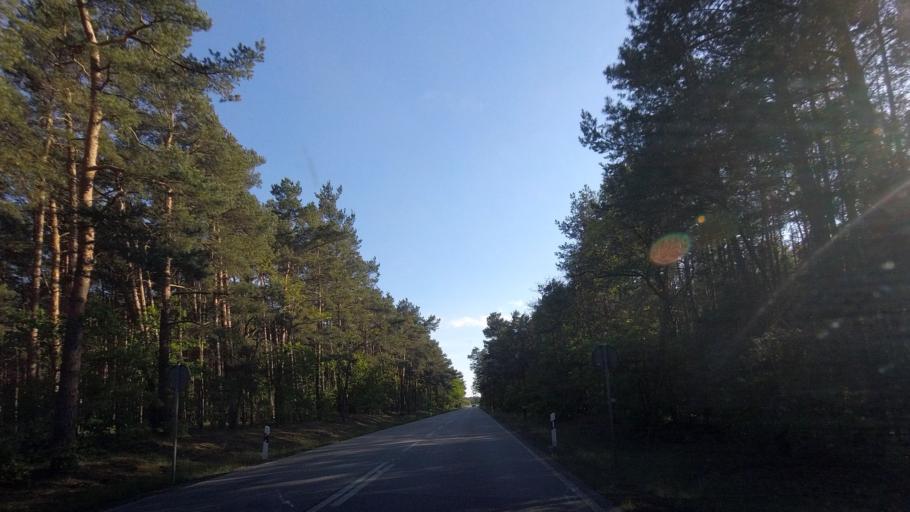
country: DE
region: Brandenburg
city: Luebben
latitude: 51.9170
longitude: 13.8692
